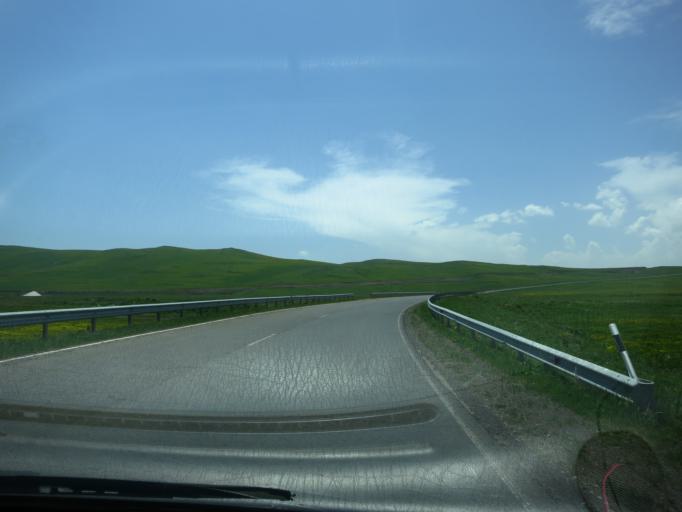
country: GE
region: Samtskhe-Javakheti
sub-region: Ninotsminda
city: Ninotsminda
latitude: 41.2975
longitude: 43.7538
